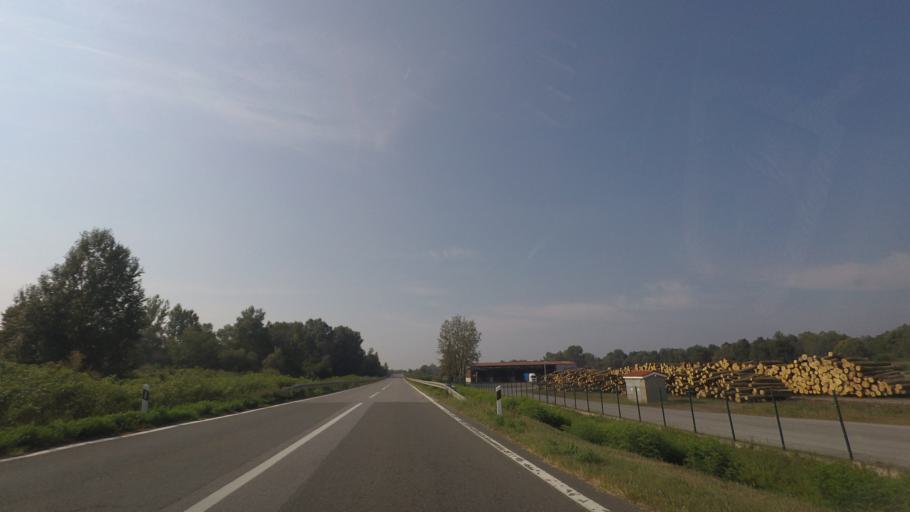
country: HR
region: Sisacko-Moslavacka
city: Novska
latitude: 45.3005
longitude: 16.9517
